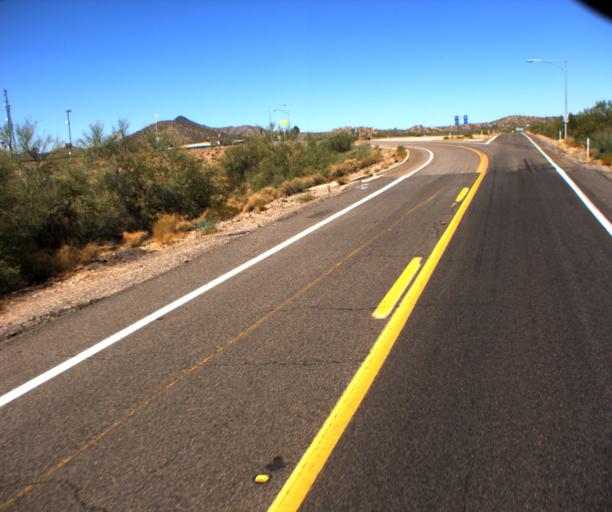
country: US
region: Arizona
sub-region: Pinal County
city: Maricopa
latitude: 32.8362
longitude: -112.1312
